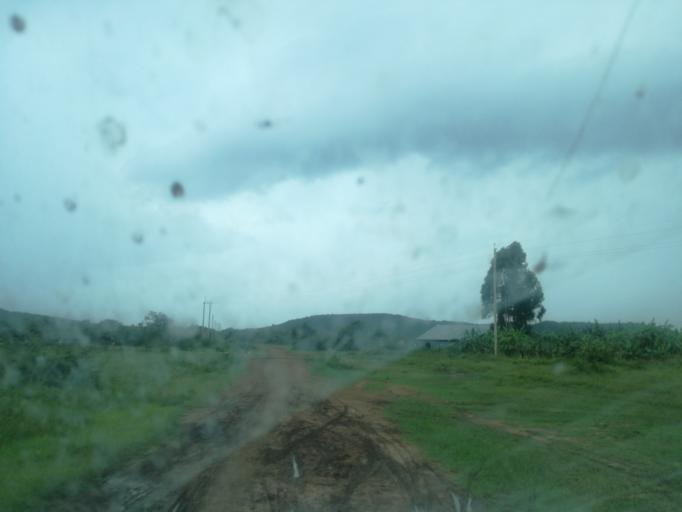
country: TZ
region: Mara
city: Mugumu
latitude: -1.8315
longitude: 34.5718
